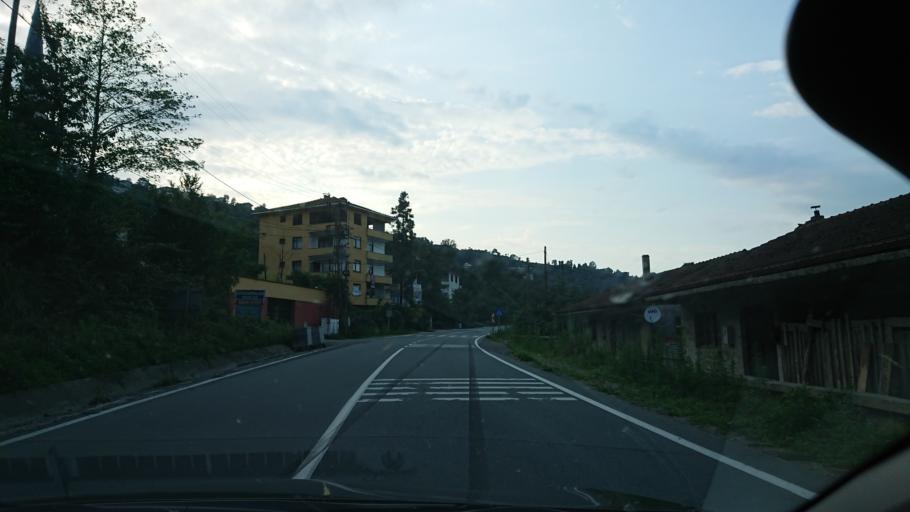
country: TR
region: Rize
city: Cayeli
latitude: 41.0661
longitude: 40.7145
